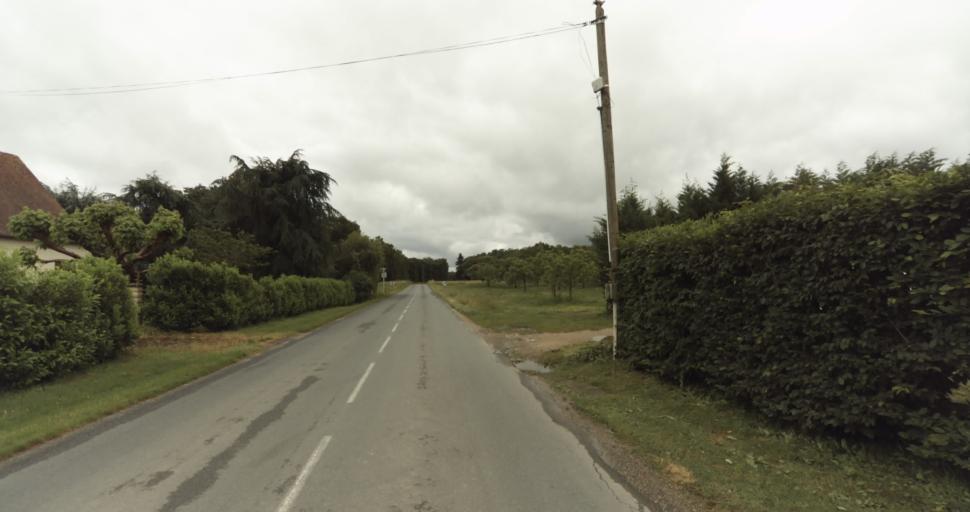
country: FR
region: Aquitaine
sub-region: Departement de la Dordogne
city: Belves
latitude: 44.6947
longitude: 0.9132
